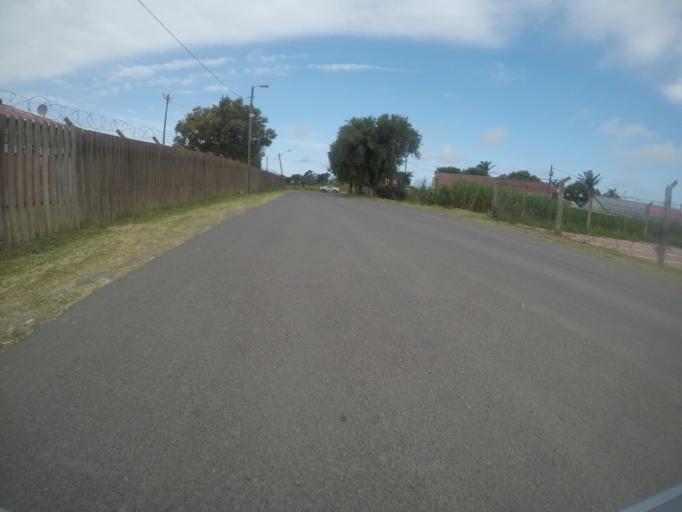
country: ZA
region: Eastern Cape
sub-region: Buffalo City Metropolitan Municipality
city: East London
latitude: -32.9920
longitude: 27.8866
